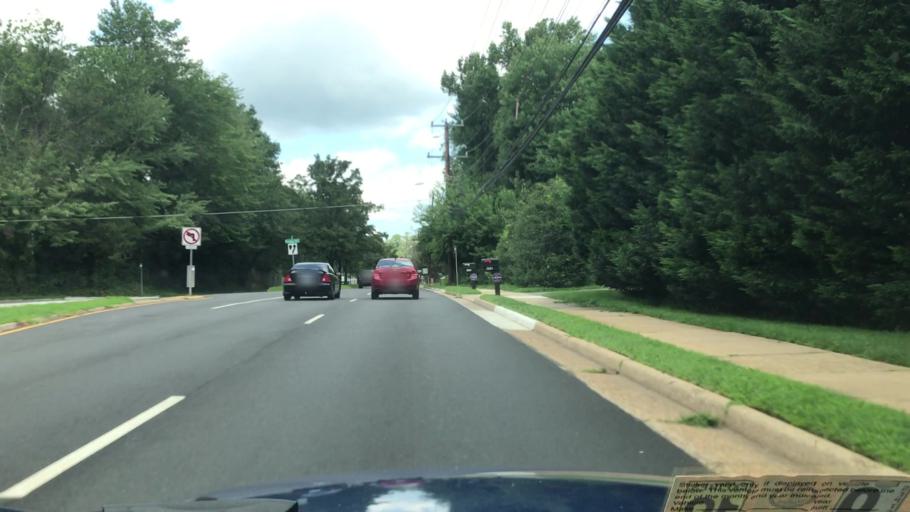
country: US
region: Virginia
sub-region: Fairfax County
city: Vienna
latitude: 38.8884
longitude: -77.2700
